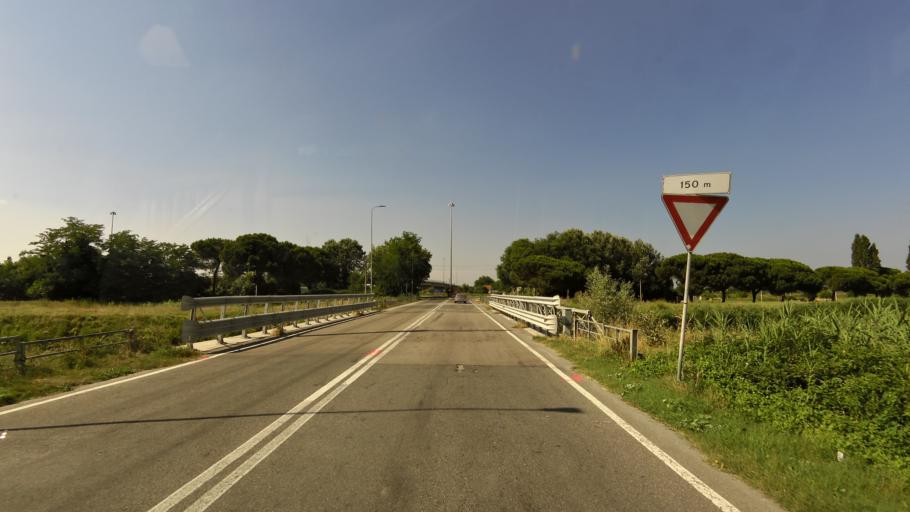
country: IT
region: Emilia-Romagna
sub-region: Provincia di Ravenna
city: Ravenna
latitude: 44.4550
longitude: 12.2094
